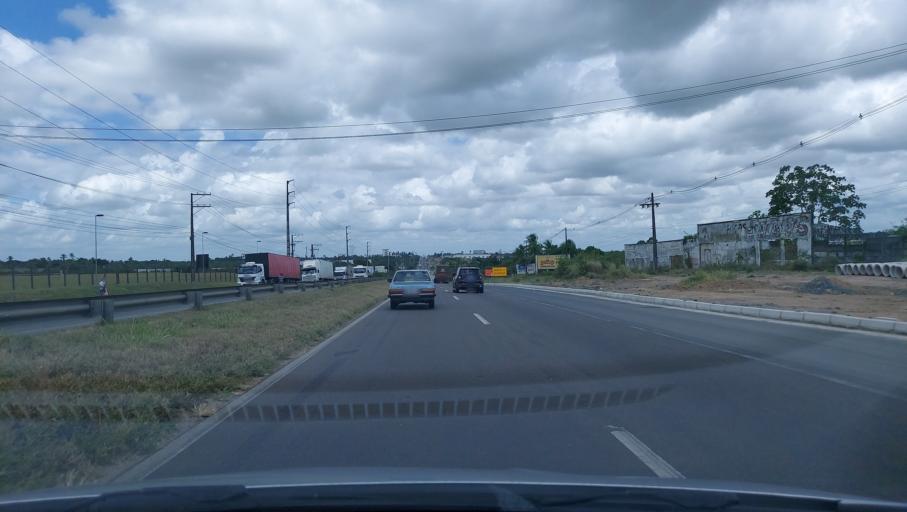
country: BR
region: Bahia
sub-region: Conceicao Do Jacuipe
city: Conceicao do Jacuipe
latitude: -12.3305
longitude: -38.8590
